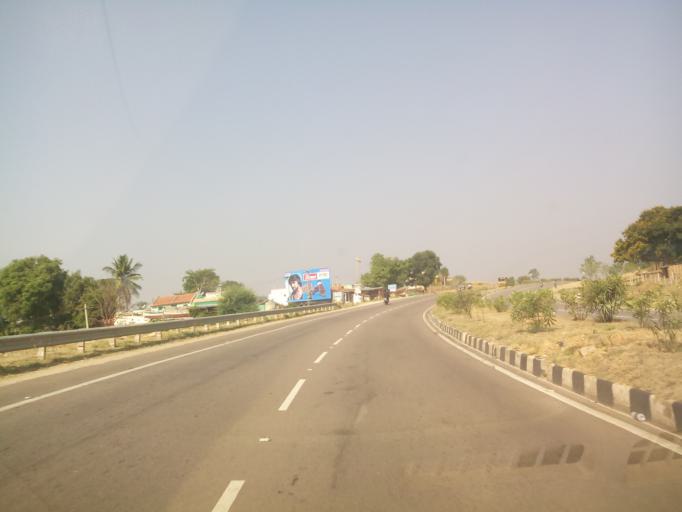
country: IN
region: Karnataka
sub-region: Tumkur
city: Kunigal
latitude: 12.9960
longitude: 76.9327
